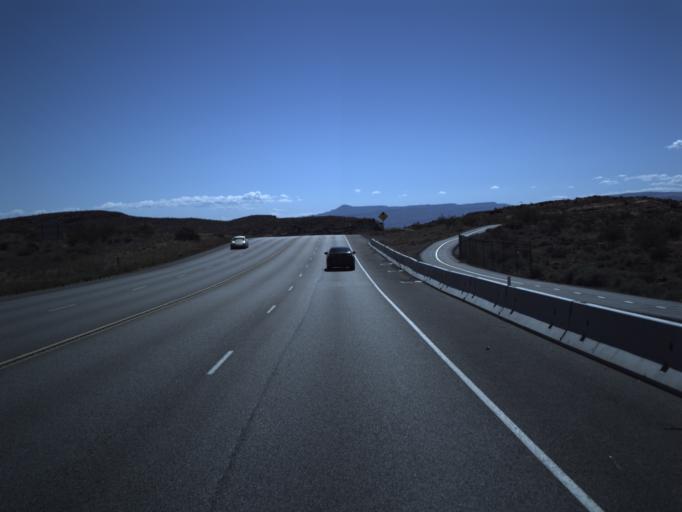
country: US
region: Utah
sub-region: Washington County
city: Saint George
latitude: 37.1429
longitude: -113.6054
